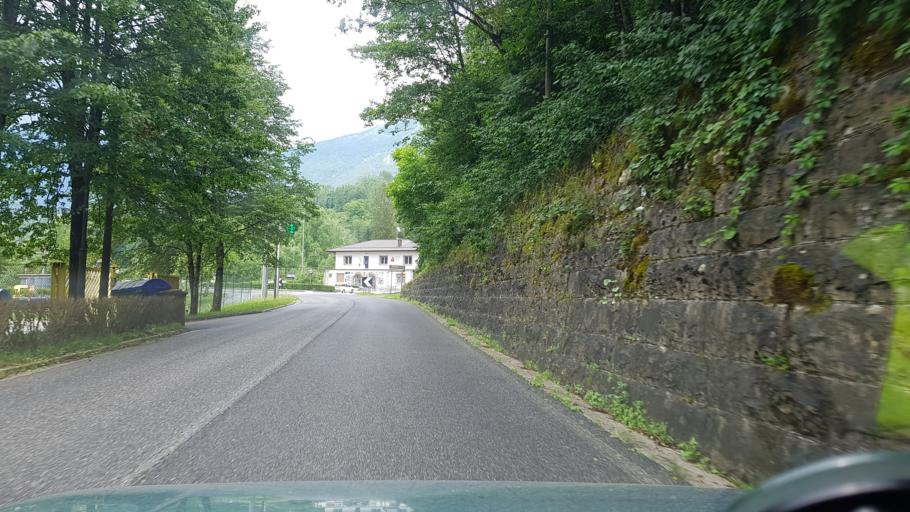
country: IT
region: Friuli Venezia Giulia
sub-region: Provincia di Udine
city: Lusevera
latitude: 46.2636
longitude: 13.2595
